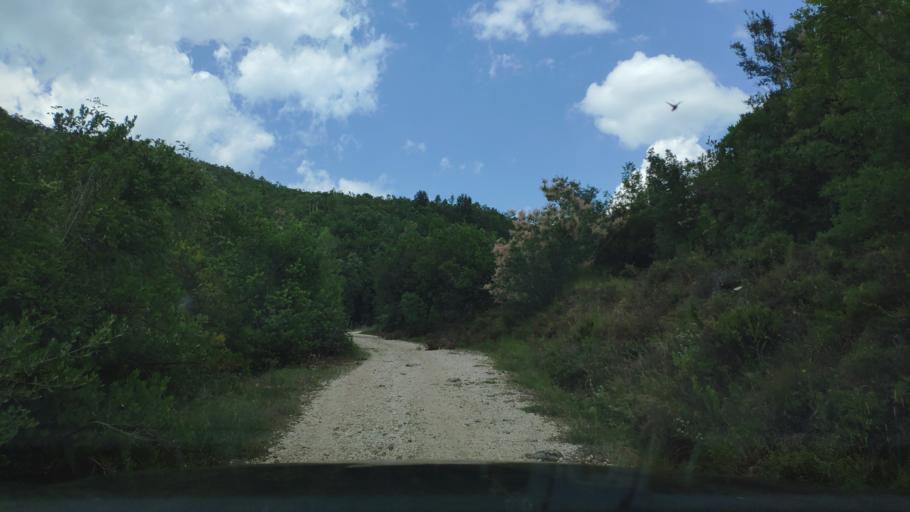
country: GR
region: Epirus
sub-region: Nomos Artas
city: Agios Dimitrios
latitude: 39.3117
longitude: 21.0177
